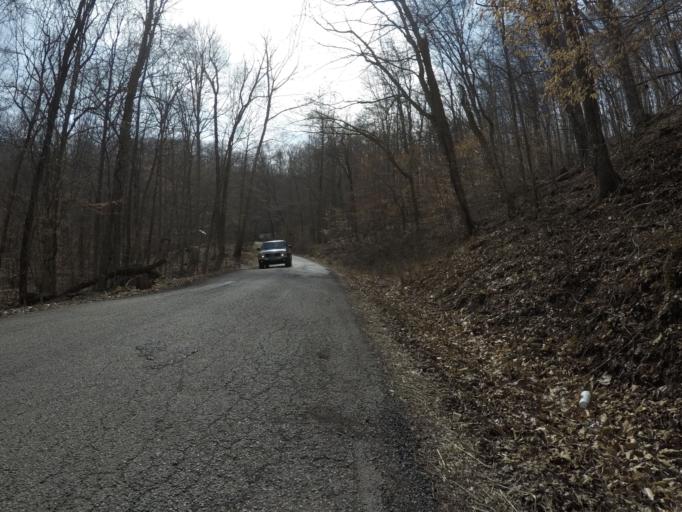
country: US
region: West Virginia
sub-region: Wayne County
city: Lavalette
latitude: 38.3433
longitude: -82.5080
